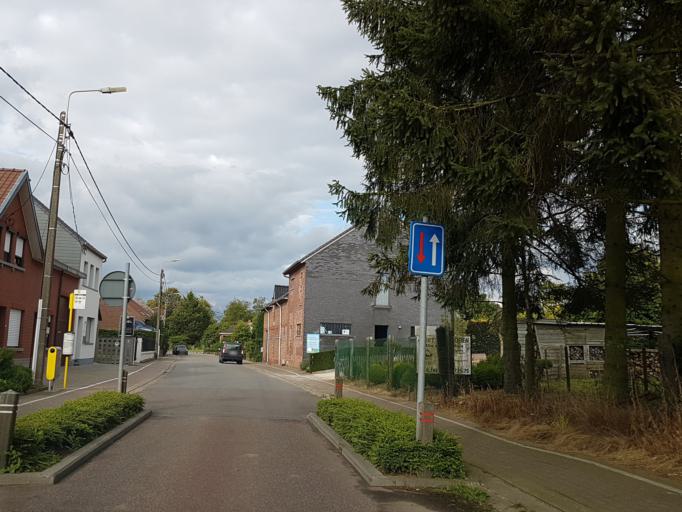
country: BE
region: Flanders
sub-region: Provincie Vlaams-Brabant
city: Kortenberg
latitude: 50.9083
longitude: 4.5896
